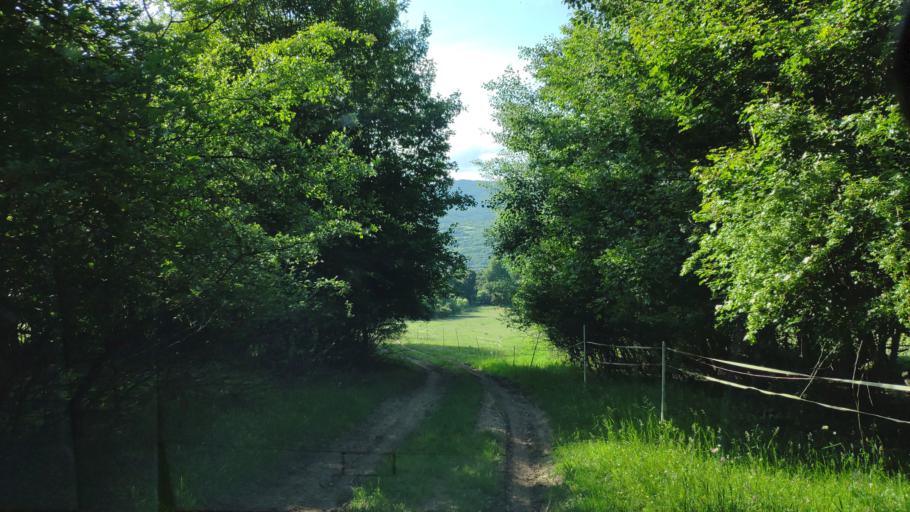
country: SK
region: Presovsky
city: Vranov nad Topl'ou
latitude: 48.8231
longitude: 21.5846
